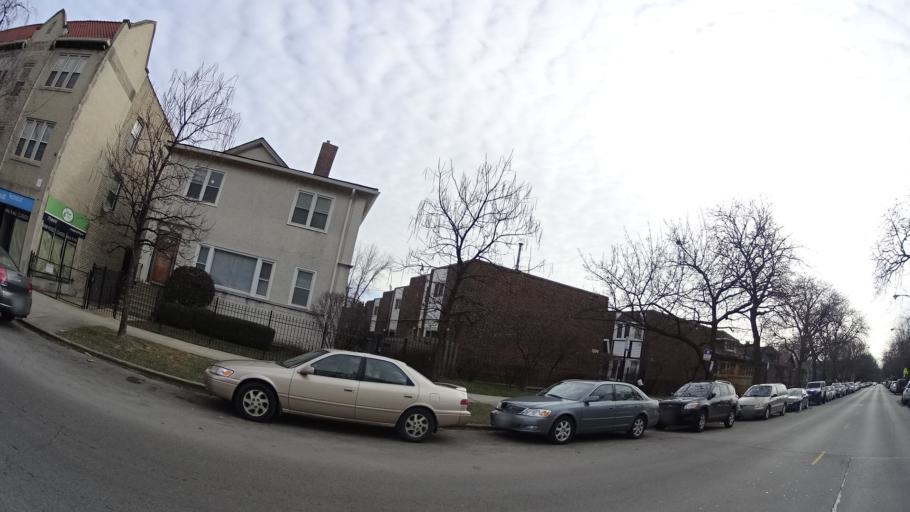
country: US
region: Illinois
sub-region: Cook County
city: Evanston
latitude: 42.0191
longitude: -87.6846
